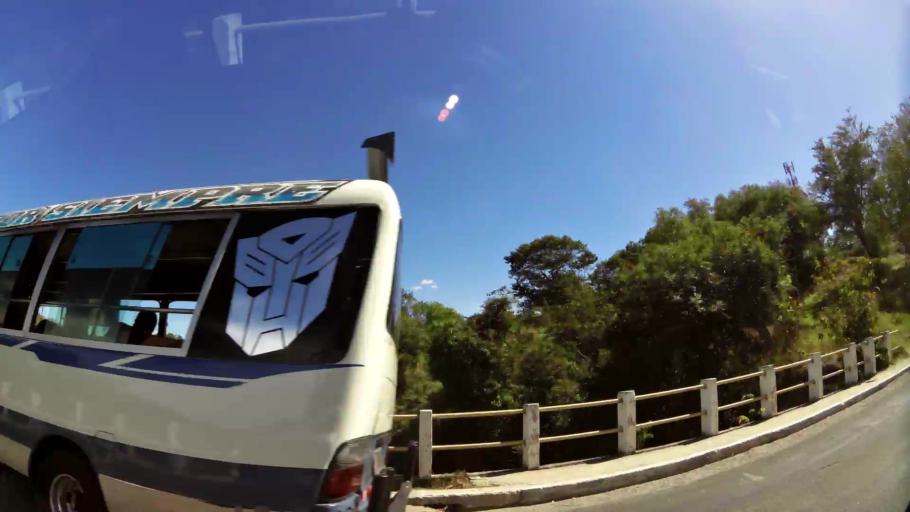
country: SV
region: San Salvador
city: Apopa
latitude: 13.8122
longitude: -89.1792
